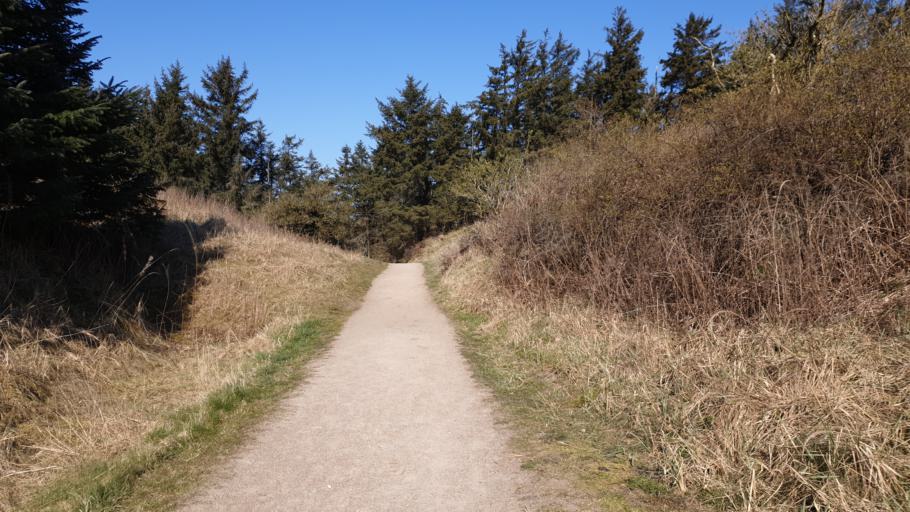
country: DK
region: North Denmark
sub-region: Hjorring Kommune
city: Hjorring
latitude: 57.4960
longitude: 9.8526
